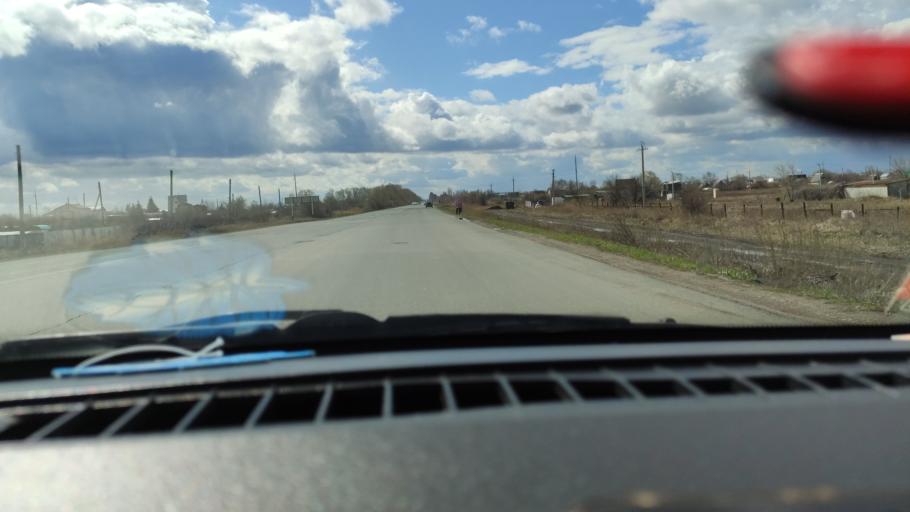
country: RU
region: Samara
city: Tol'yatti
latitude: 53.7088
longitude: 49.4229
